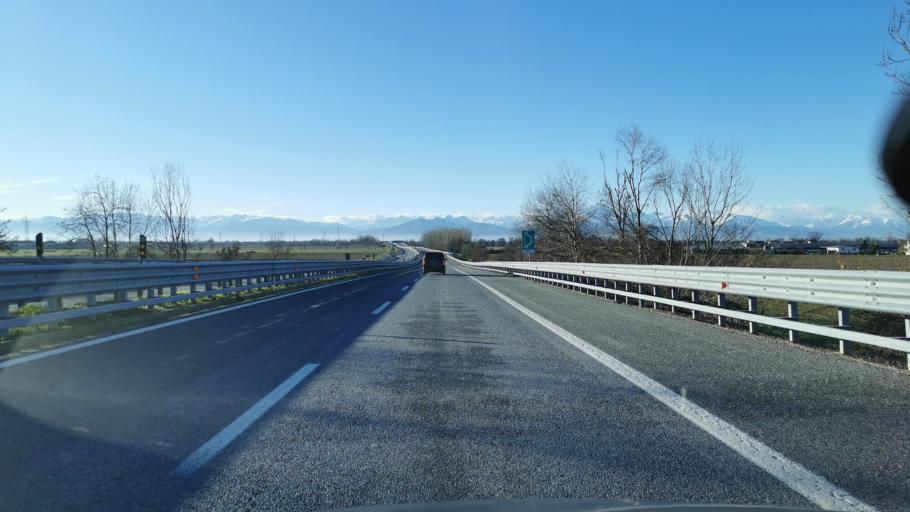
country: IT
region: Piedmont
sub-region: Provincia di Cuneo
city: Trinita
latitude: 44.4685
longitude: 7.7663
